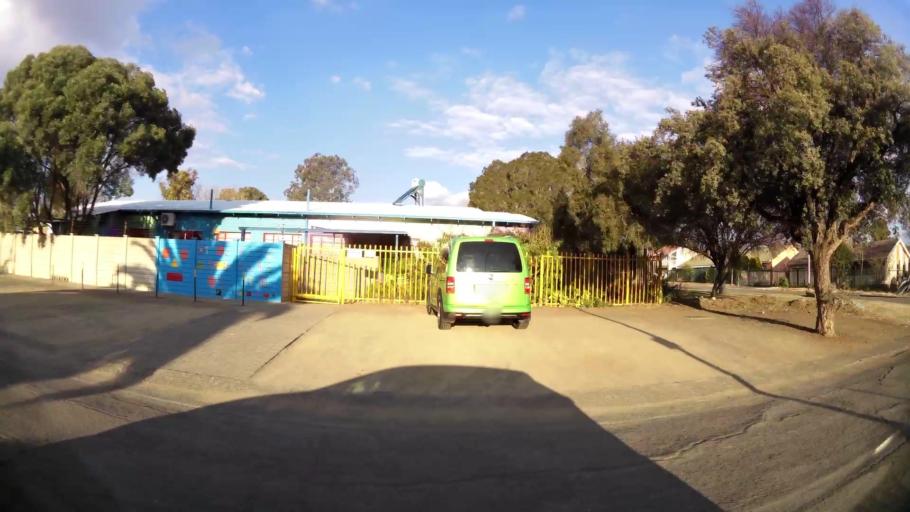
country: ZA
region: Orange Free State
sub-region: Mangaung Metropolitan Municipality
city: Bloemfontein
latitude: -29.1466
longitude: 26.1896
